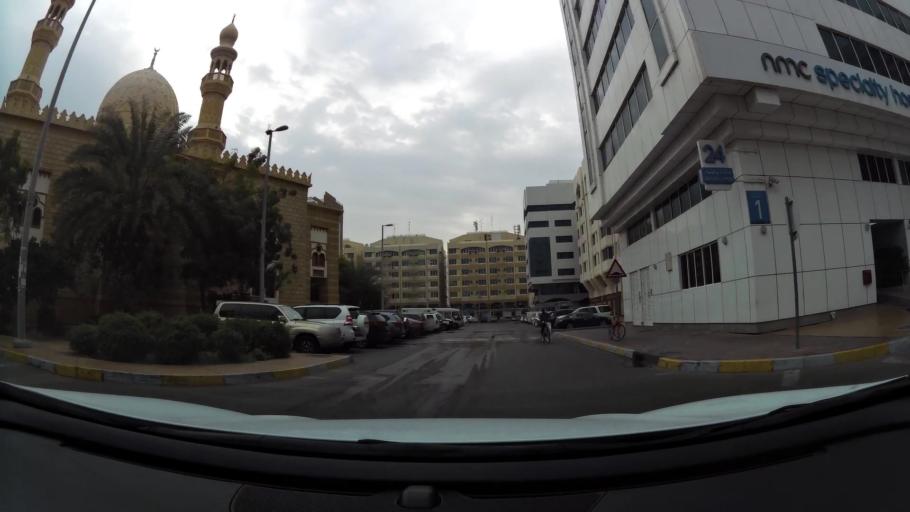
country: AE
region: Abu Dhabi
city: Abu Dhabi
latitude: 24.4827
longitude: 54.3615
